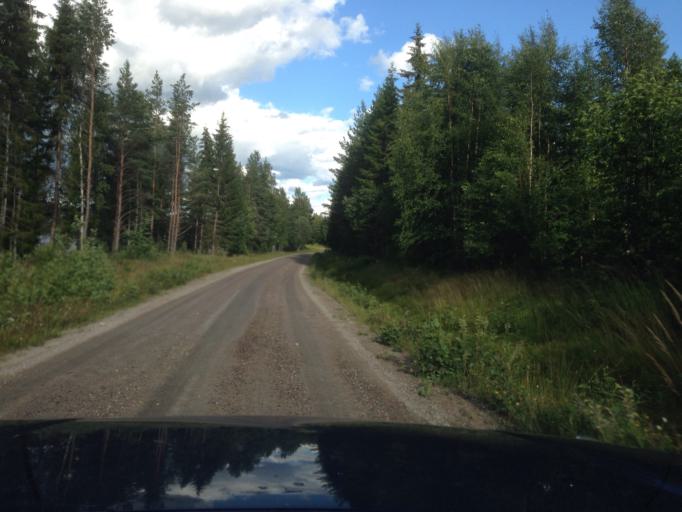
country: SE
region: Dalarna
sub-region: Ludvika Kommun
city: Abborrberget
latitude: 60.3114
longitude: 14.6595
